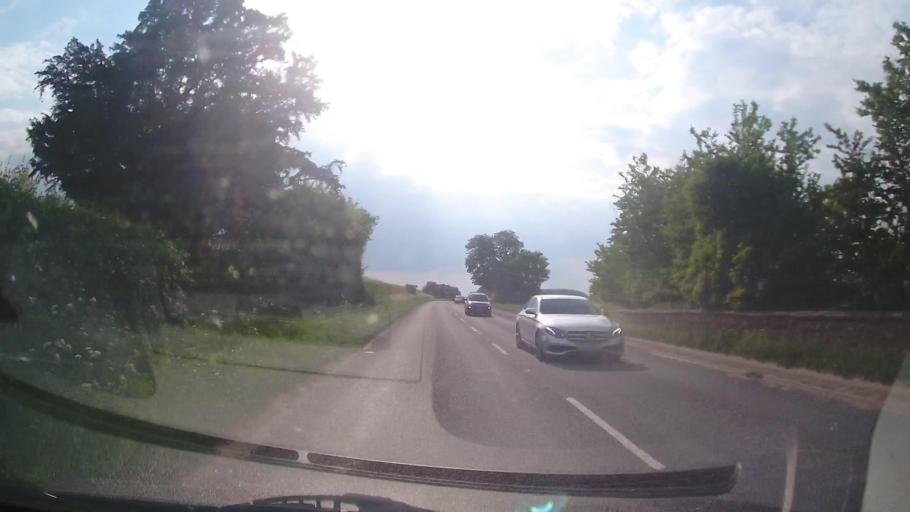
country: GB
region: England
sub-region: Telford and Wrekin
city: Wellington
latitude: 52.6923
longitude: -2.5468
